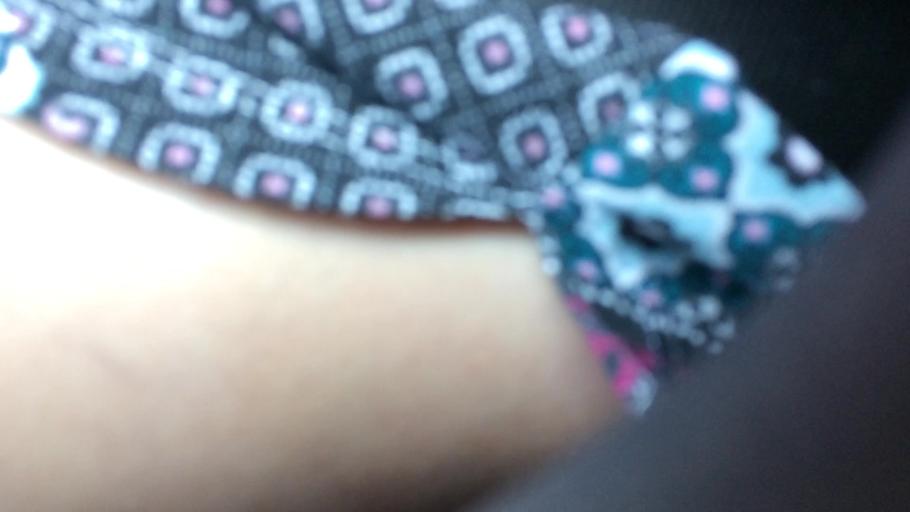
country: US
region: New Mexico
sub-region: San Miguel County
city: Las Vegas
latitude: 35.7969
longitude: -104.9848
